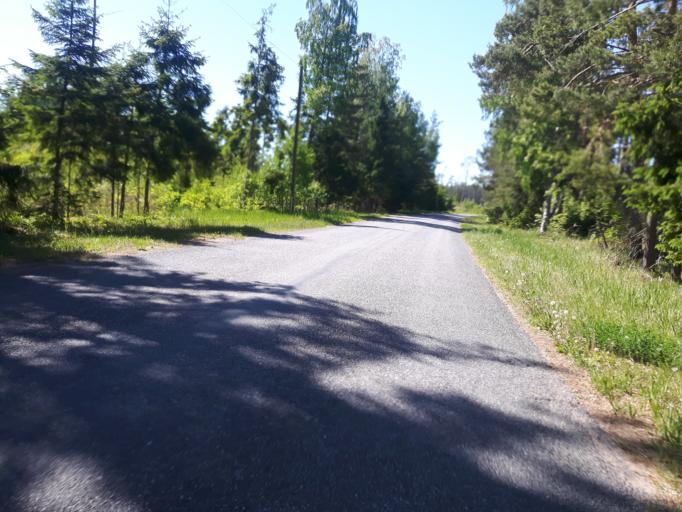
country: EE
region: Laeaene-Virumaa
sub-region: Haljala vald
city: Haljala
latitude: 59.5695
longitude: 26.2942
